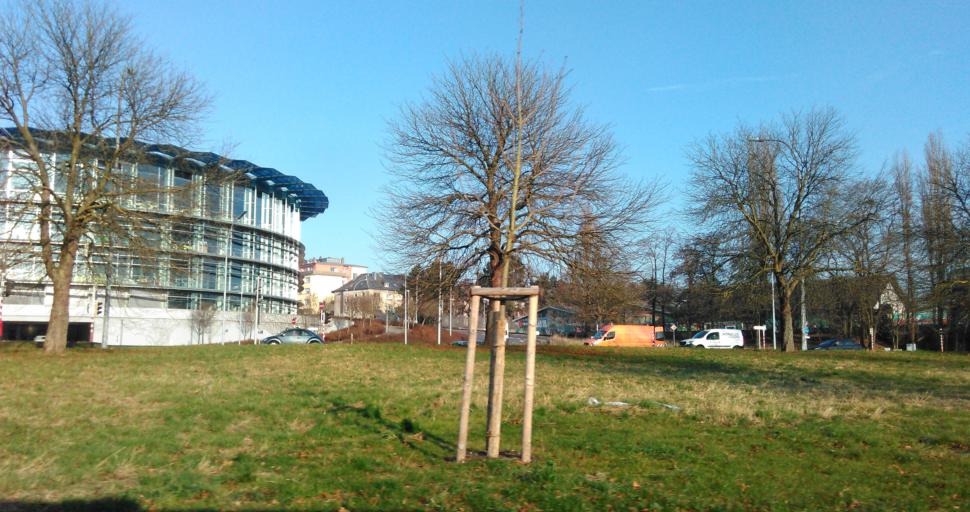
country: LU
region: Luxembourg
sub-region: Canton de Luxembourg
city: Luxembourg
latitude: 49.5995
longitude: 6.1138
